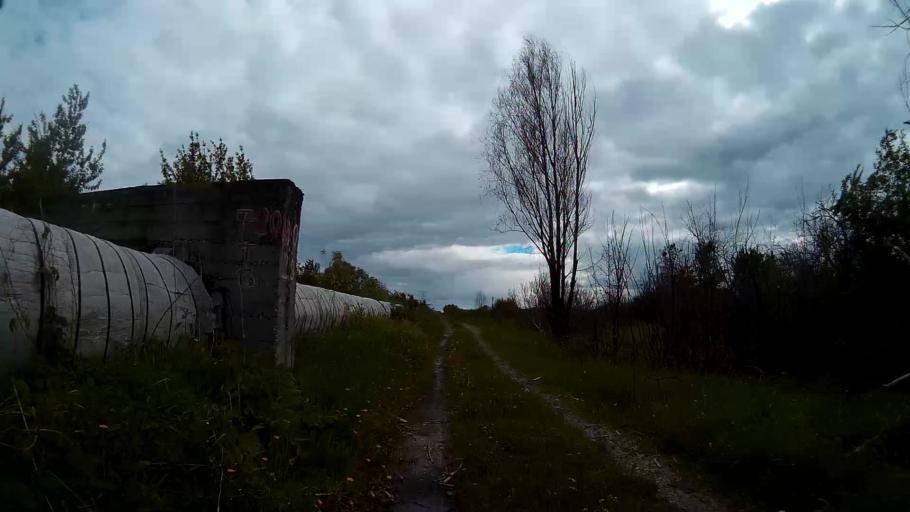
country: RU
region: Ulyanovsk
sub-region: Ulyanovskiy Rayon
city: Ulyanovsk
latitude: 54.2444
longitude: 48.3000
